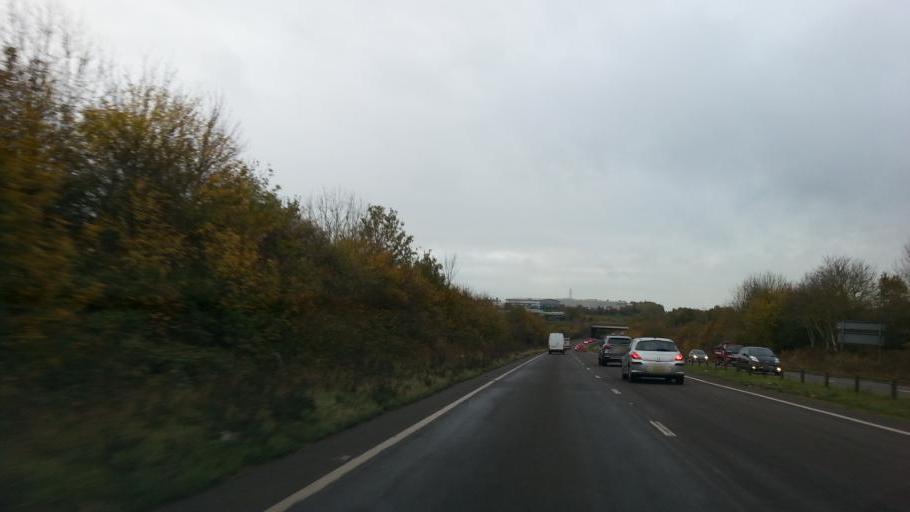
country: GB
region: England
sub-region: Northamptonshire
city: Kettering
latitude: 52.4188
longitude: -0.7311
